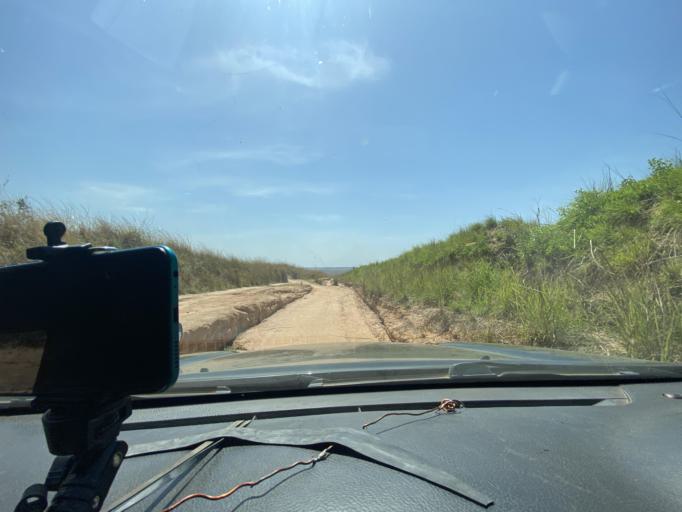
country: CD
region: Kasai-Oriental
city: Kabinda
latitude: -5.9476
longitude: 24.8065
